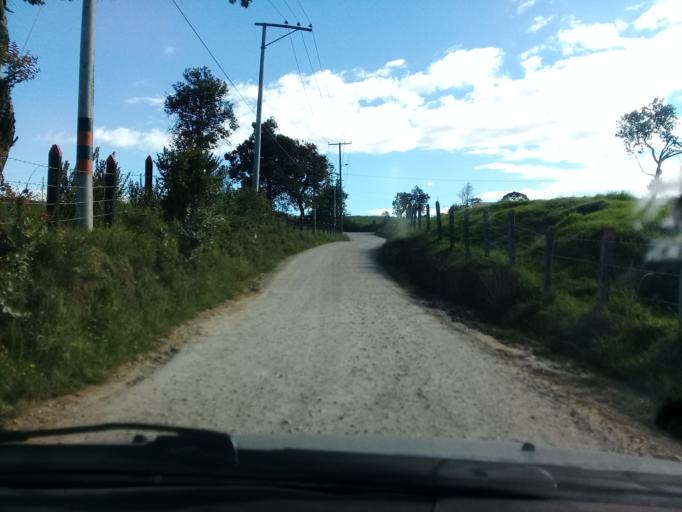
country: CO
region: Cundinamarca
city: Zipaquira
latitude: 4.9966
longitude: -74.0695
